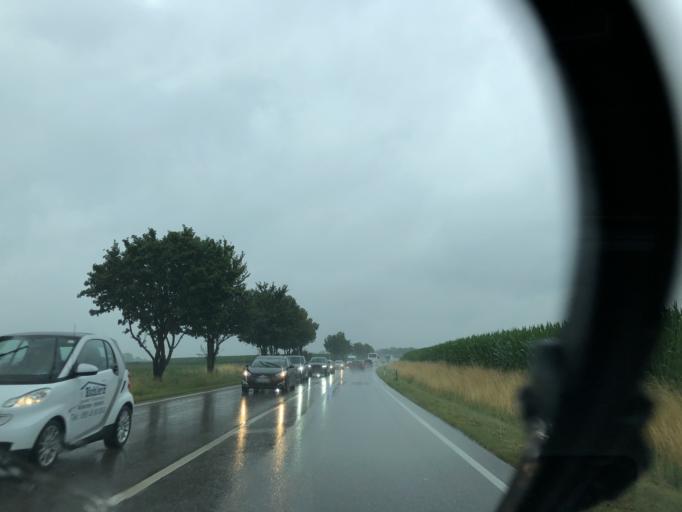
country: DE
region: Bavaria
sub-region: Upper Bavaria
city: Oberding
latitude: 48.3268
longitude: 11.8801
